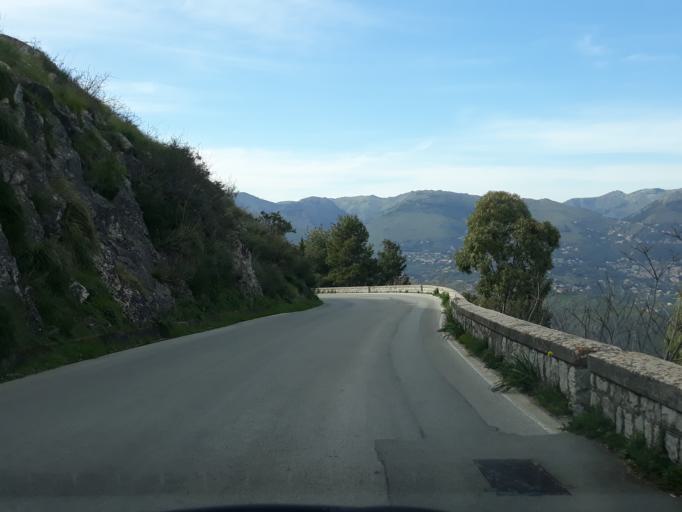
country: IT
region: Sicily
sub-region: Palermo
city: Piano Maglio-Blandino
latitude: 38.0445
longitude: 13.3088
